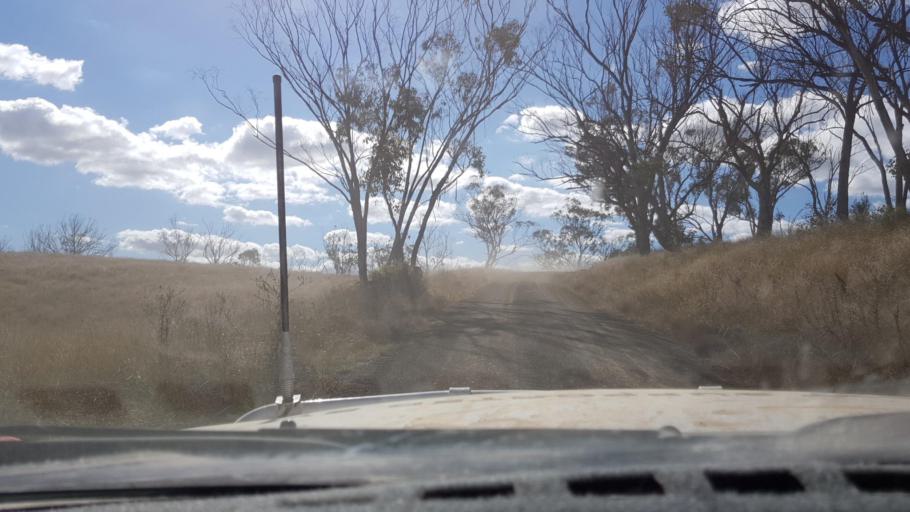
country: AU
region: New South Wales
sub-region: Tamworth Municipality
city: Manilla
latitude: -30.4705
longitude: 150.7756
